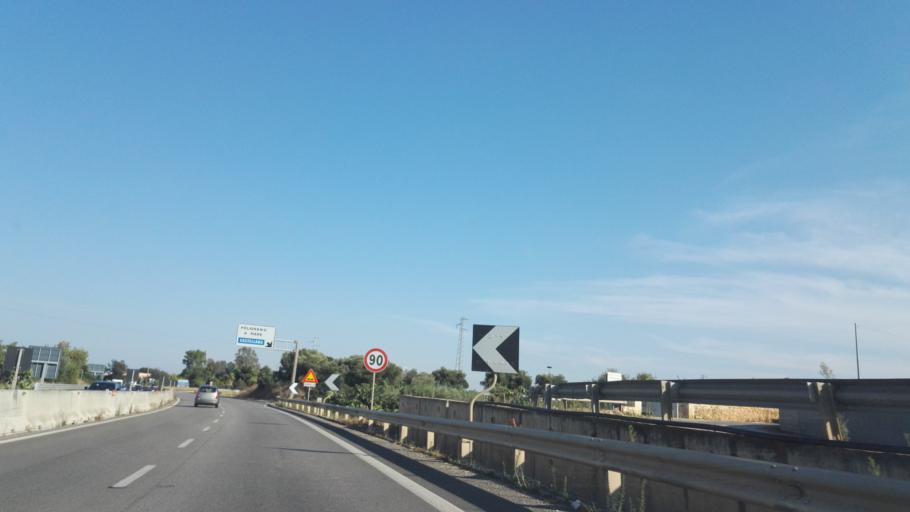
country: IT
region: Apulia
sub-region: Provincia di Bari
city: Polignano a Mare
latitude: 40.9896
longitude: 17.2091
